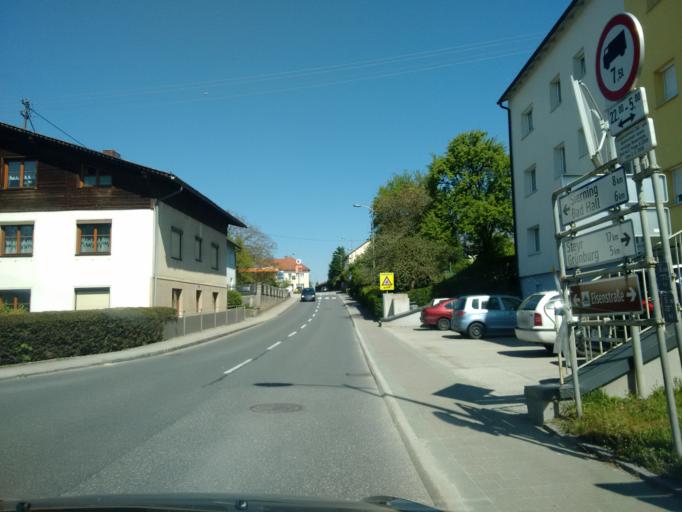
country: AT
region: Upper Austria
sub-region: Politischer Bezirk Steyr-Land
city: Waldneukirchen
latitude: 47.9981
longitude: 14.2604
